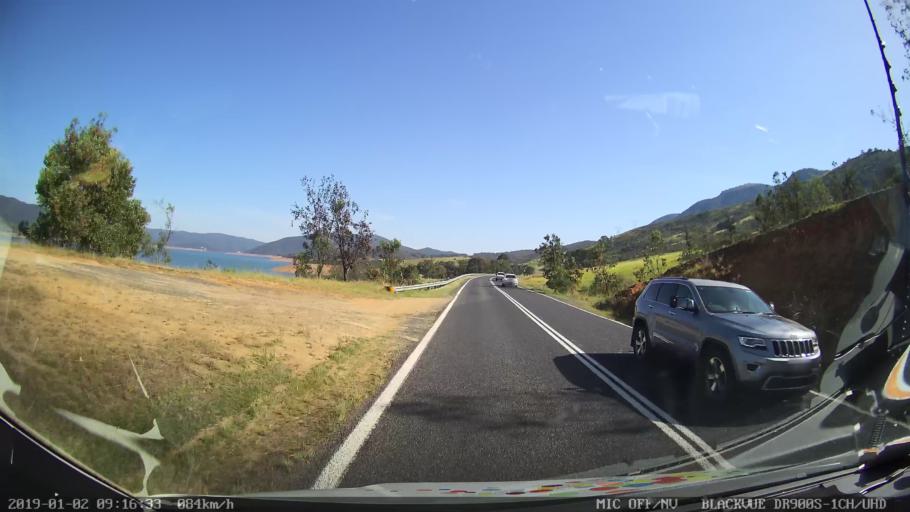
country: AU
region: New South Wales
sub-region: Tumut Shire
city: Tumut
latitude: -35.4520
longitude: 148.2843
